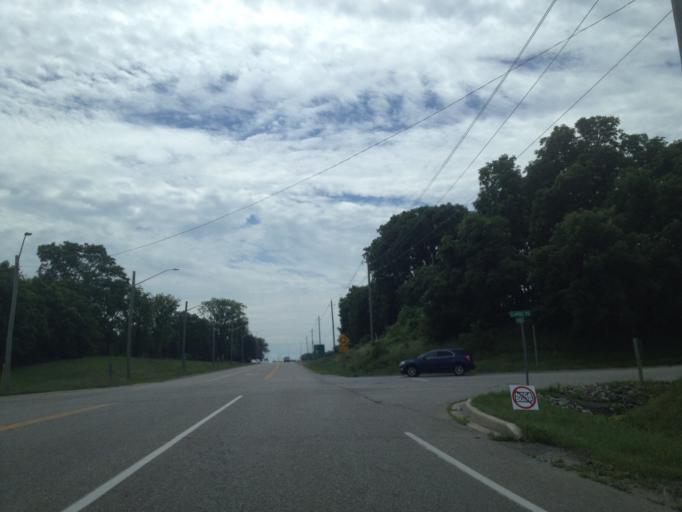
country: CA
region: Ontario
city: Ingersoll
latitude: 43.0321
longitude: -80.8603
